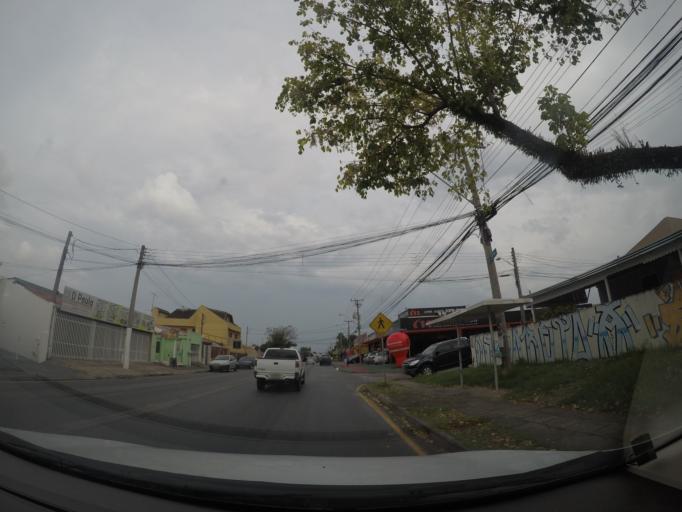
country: BR
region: Parana
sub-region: Sao Jose Dos Pinhais
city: Sao Jose dos Pinhais
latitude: -25.5288
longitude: -49.2599
